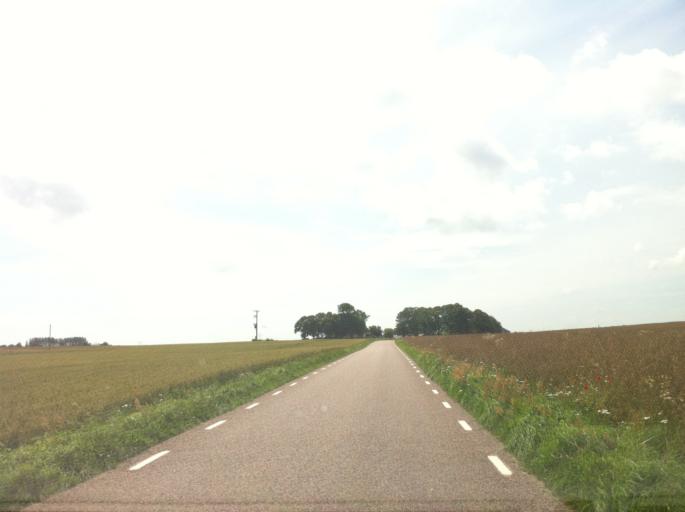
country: SE
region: Skane
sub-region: Skurups Kommun
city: Skurup
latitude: 55.4285
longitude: 13.4518
